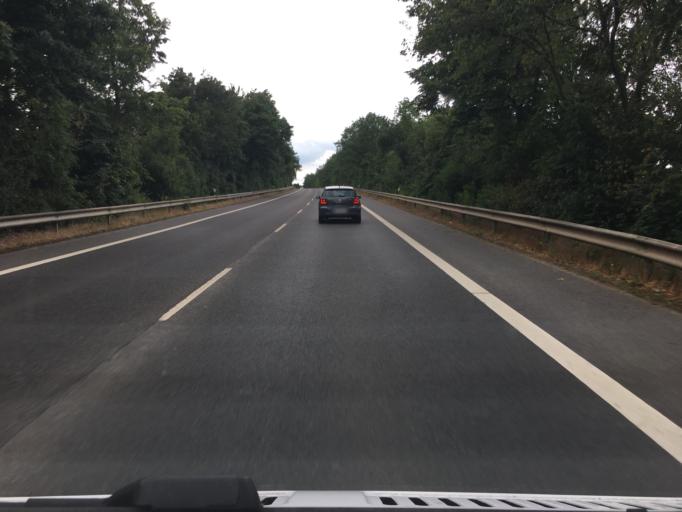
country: DE
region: North Rhine-Westphalia
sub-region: Regierungsbezirk Dusseldorf
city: Dormagen
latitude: 51.1063
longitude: 6.8107
